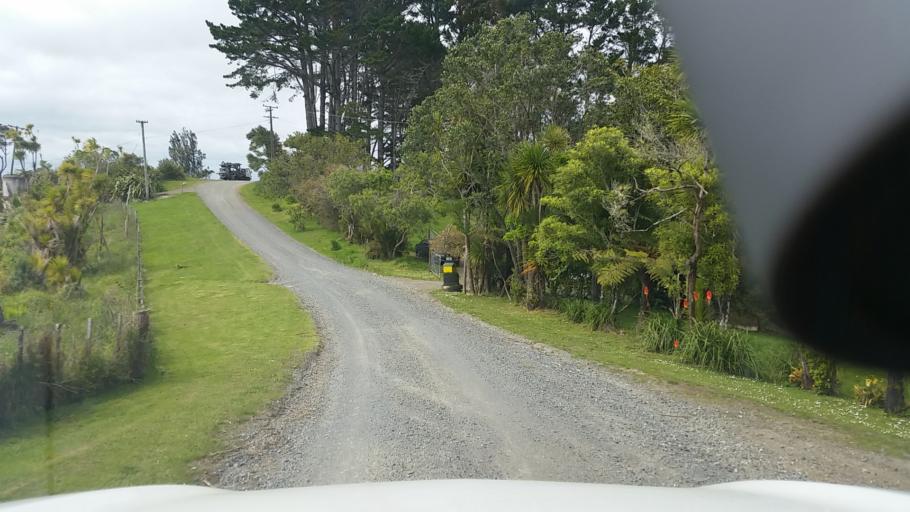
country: NZ
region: Auckland
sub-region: Auckland
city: Muriwai Beach
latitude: -36.8414
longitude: 174.5119
